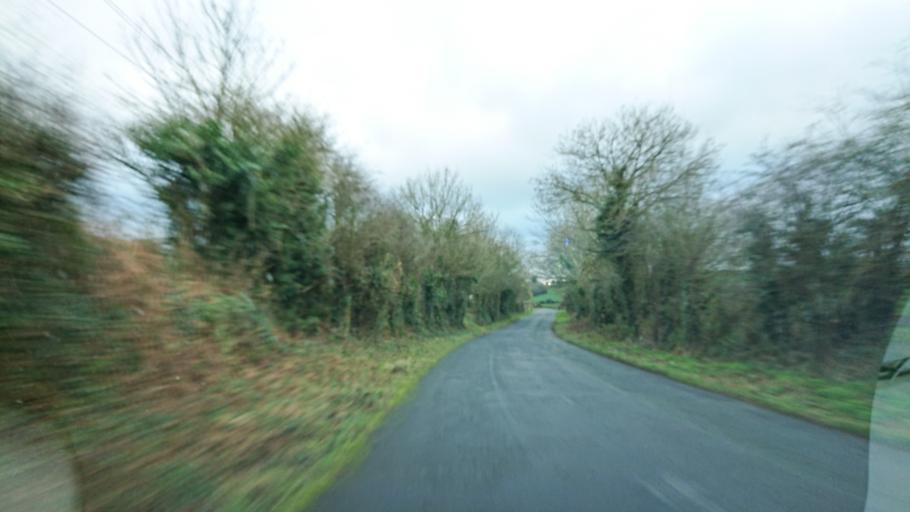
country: IE
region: Munster
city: Carrick-on-Suir
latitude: 52.2453
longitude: -7.4155
